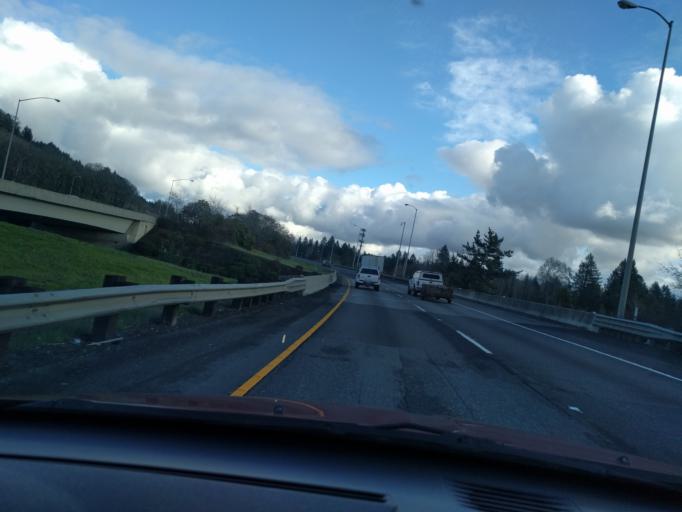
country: US
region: Oregon
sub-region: Clackamas County
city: West Linn
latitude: 45.3477
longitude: -122.6526
